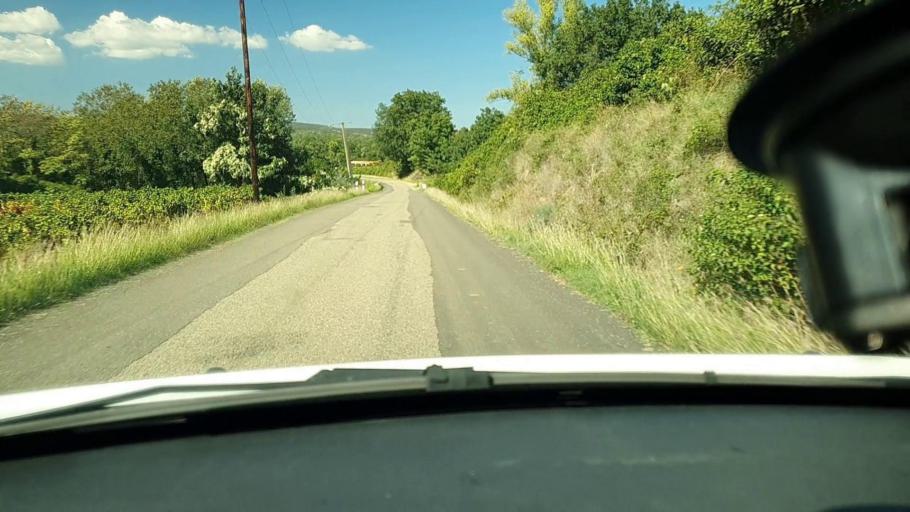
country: FR
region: Languedoc-Roussillon
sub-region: Departement du Gard
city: Goudargues
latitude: 44.1798
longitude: 4.4885
